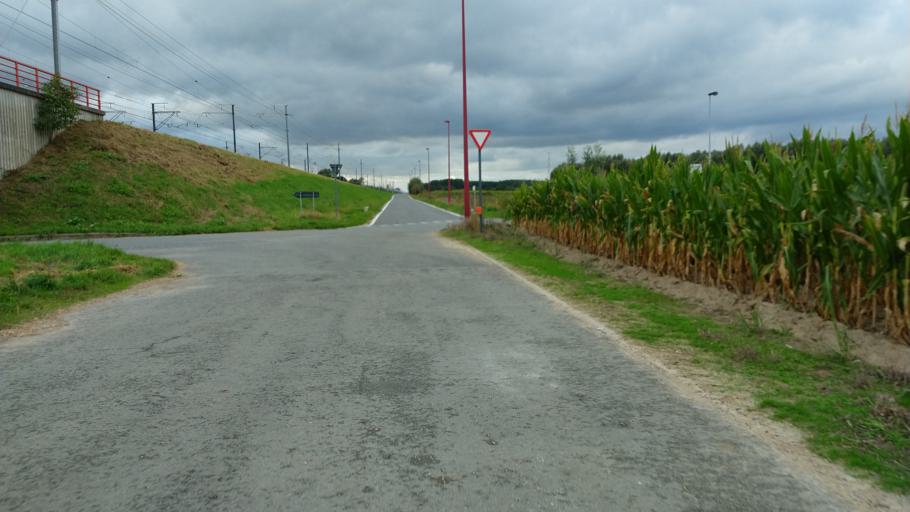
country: BE
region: Flanders
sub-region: Provincie Oost-Vlaanderen
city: Nevele
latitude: 51.0669
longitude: 3.5663
